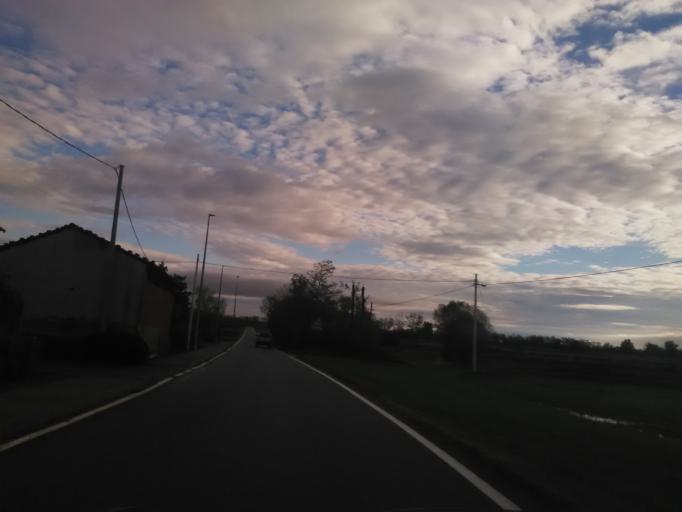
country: IT
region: Piedmont
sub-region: Provincia di Vercelli
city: Rovasenda
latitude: 45.5392
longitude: 8.3237
